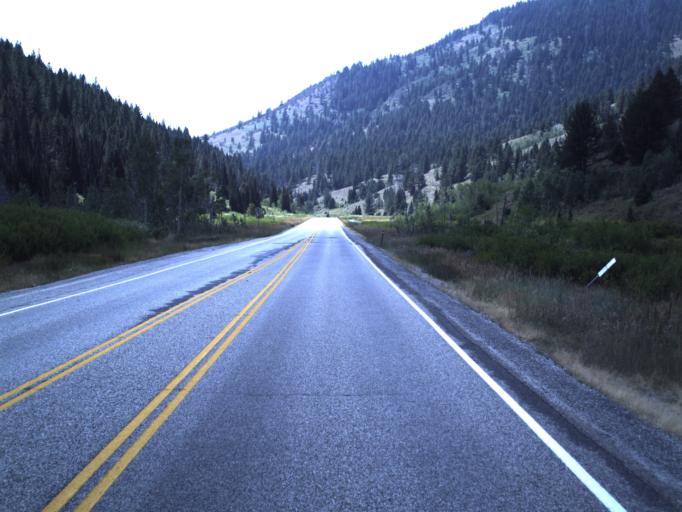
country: US
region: Utah
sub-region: Cache County
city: Richmond
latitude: 41.9616
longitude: -111.5337
